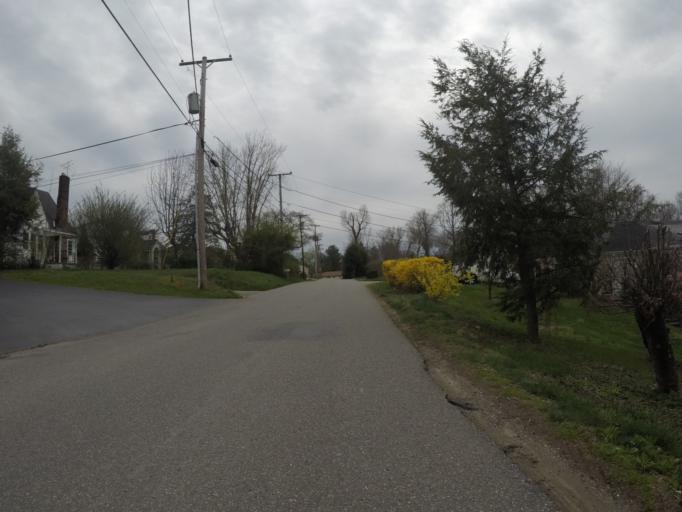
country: US
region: West Virginia
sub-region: Cabell County
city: Pea Ridge
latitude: 38.4164
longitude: -82.3210
